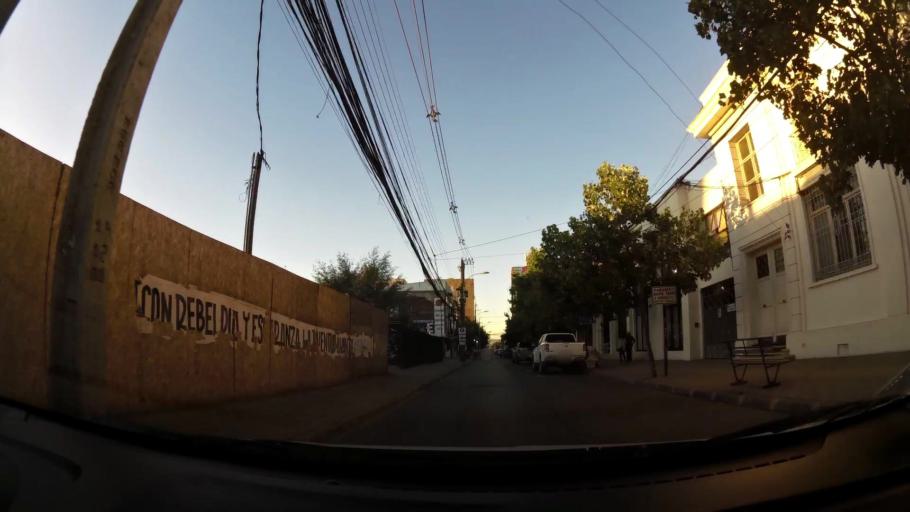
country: CL
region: Maule
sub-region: Provincia de Curico
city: Curico
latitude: -34.9844
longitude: -71.2389
